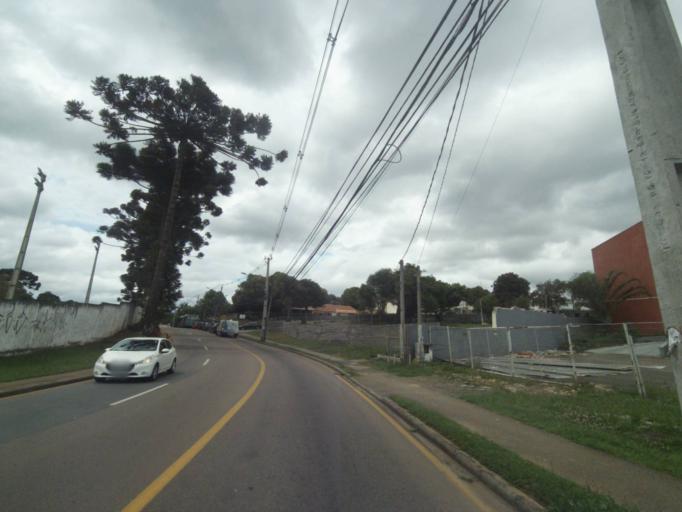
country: BR
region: Parana
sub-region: Curitiba
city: Curitiba
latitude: -25.3890
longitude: -49.2833
